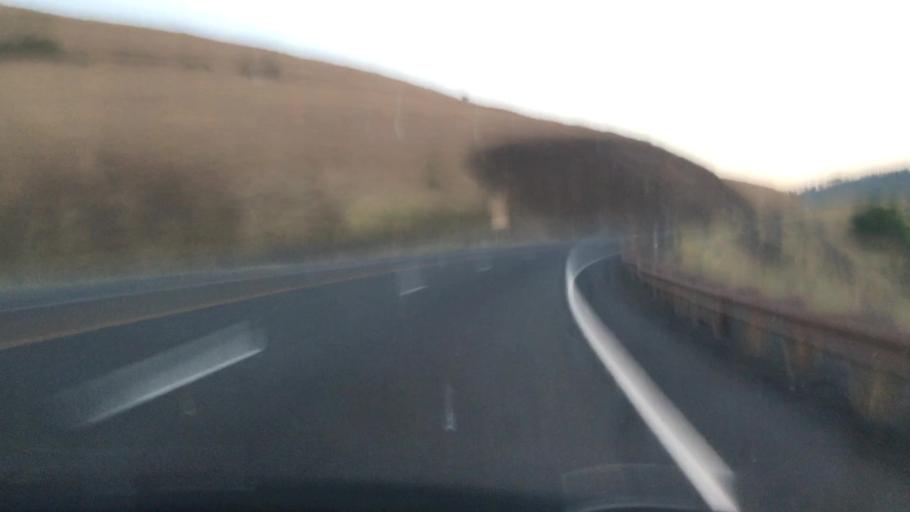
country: US
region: Idaho
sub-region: Idaho County
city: Grangeville
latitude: 45.8279
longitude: -116.2534
